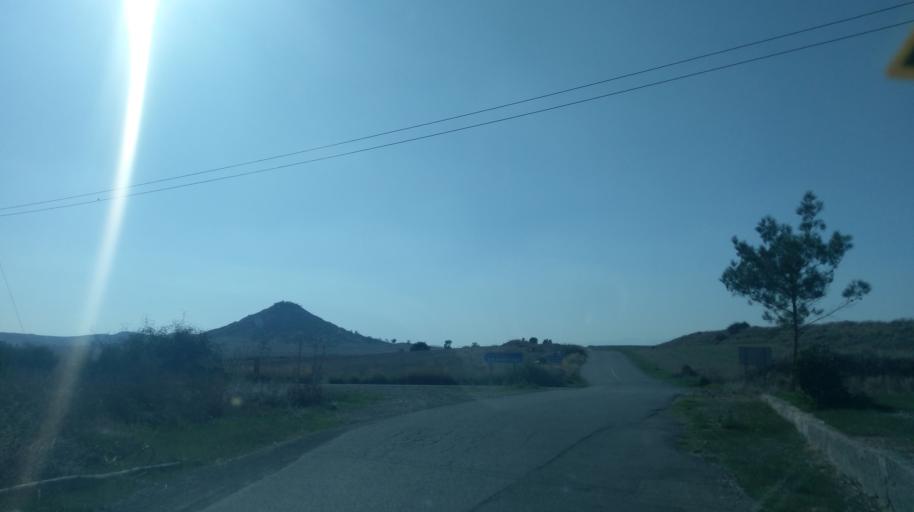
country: CY
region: Larnaka
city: Athienou
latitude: 35.0743
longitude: 33.4909
